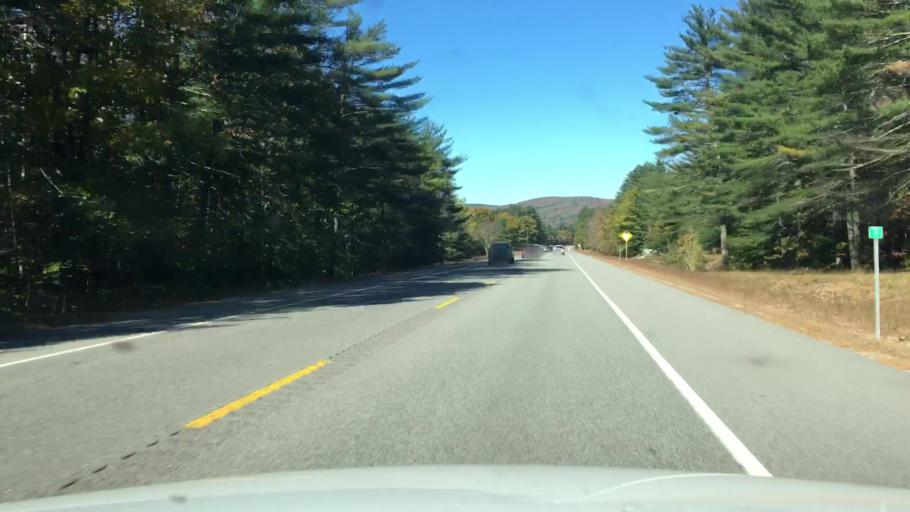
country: US
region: New Hampshire
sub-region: Carroll County
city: Sanbornville
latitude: 43.4920
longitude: -71.0174
